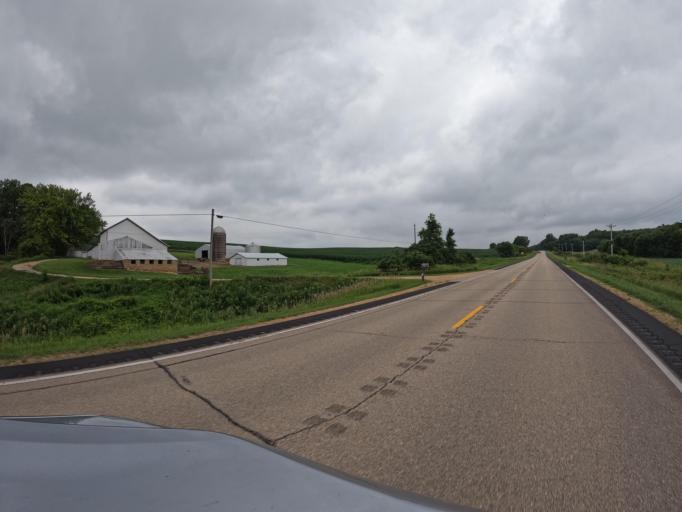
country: US
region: Illinois
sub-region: Carroll County
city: Savanna
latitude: 42.0119
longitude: -90.1830
